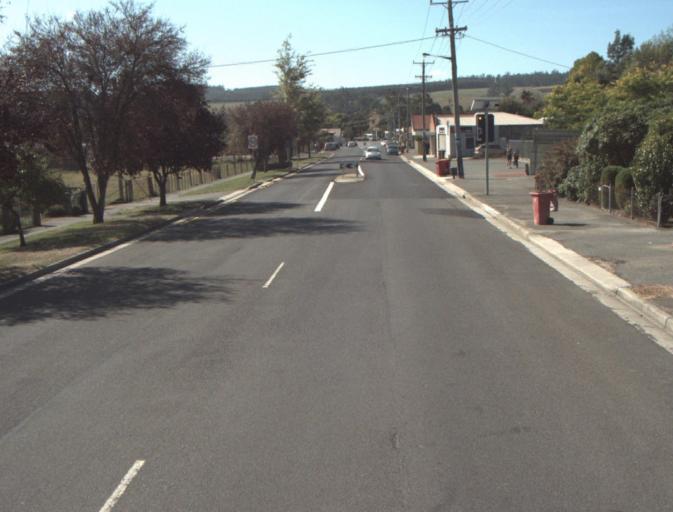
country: AU
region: Tasmania
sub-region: Launceston
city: Mayfield
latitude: -41.2522
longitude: 147.2163
